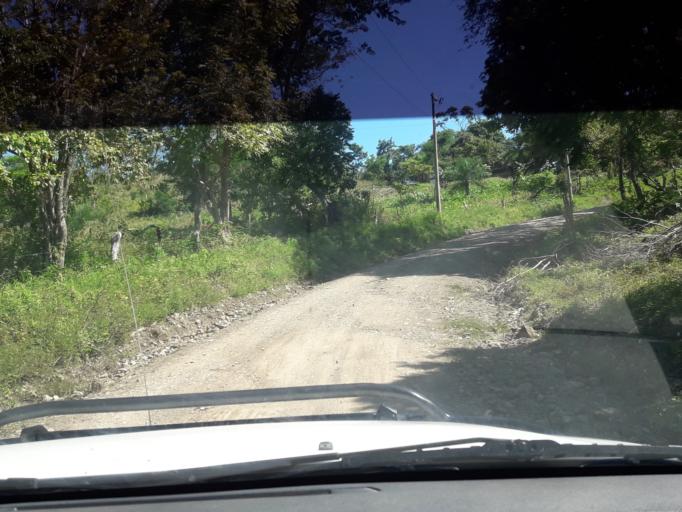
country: NI
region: Rivas
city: Cardenas
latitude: 11.2222
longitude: -85.6469
